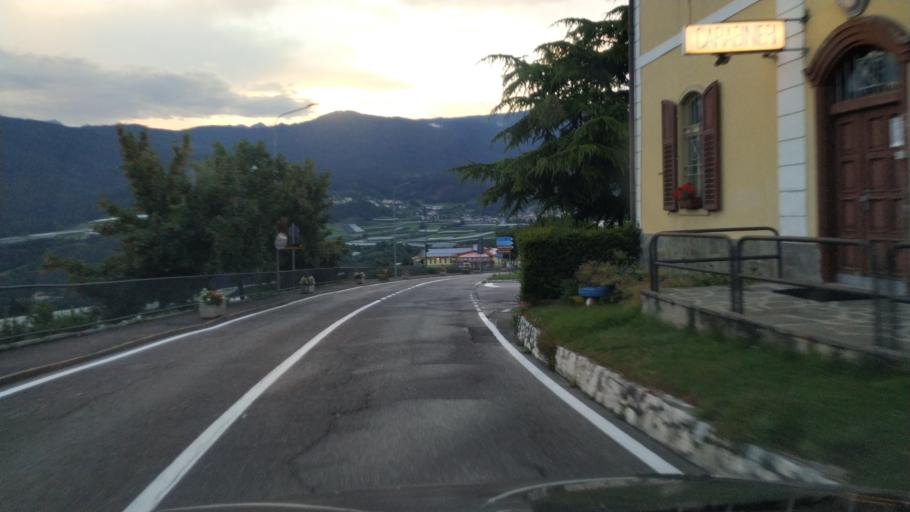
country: IT
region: Trentino-Alto Adige
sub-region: Provincia di Trento
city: Fondo
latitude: 46.4388
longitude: 11.1337
